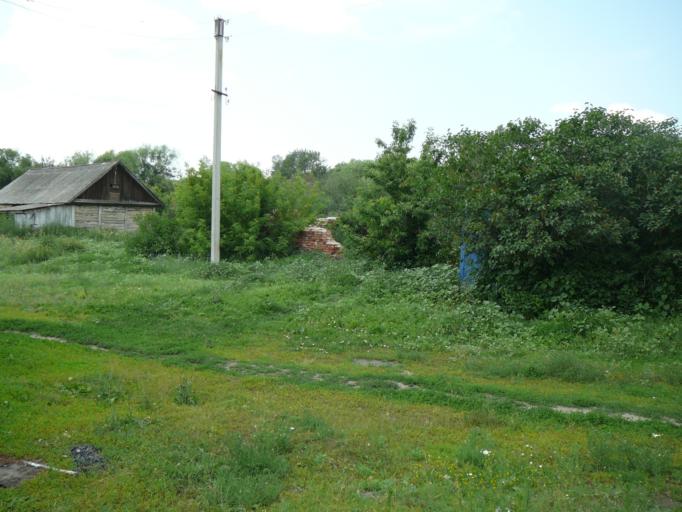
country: RU
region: Penza
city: Tamala
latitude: 52.3865
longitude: 43.3928
